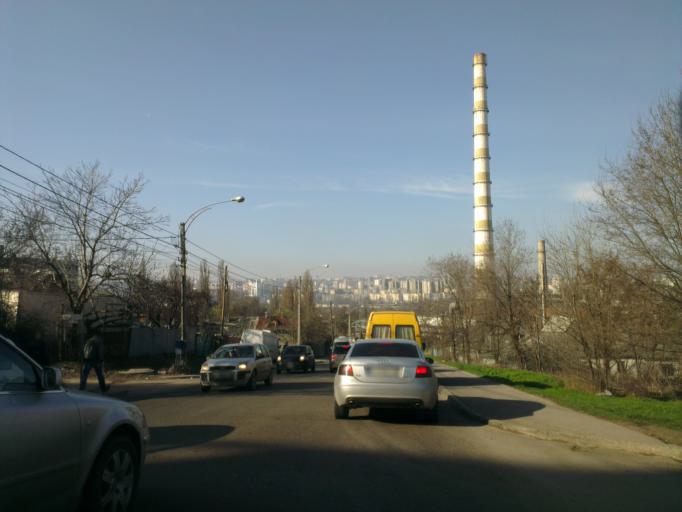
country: MD
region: Chisinau
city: Chisinau
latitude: 47.0269
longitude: 28.8713
